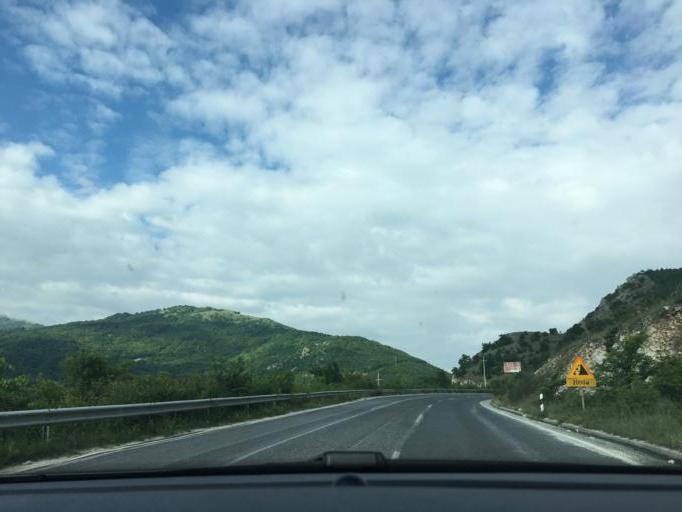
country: MK
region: Prilep
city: Prilep
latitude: 41.3701
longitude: 21.6766
